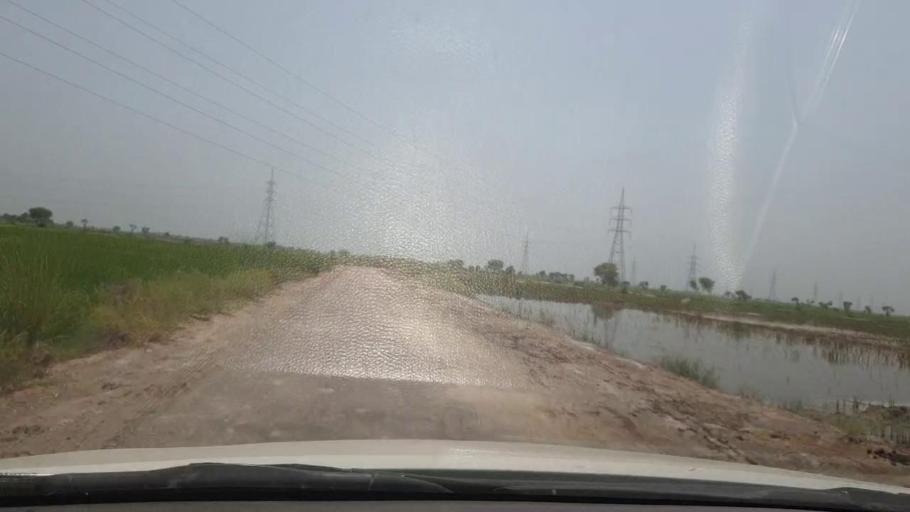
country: PK
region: Sindh
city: Shikarpur
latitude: 28.0937
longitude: 68.6170
